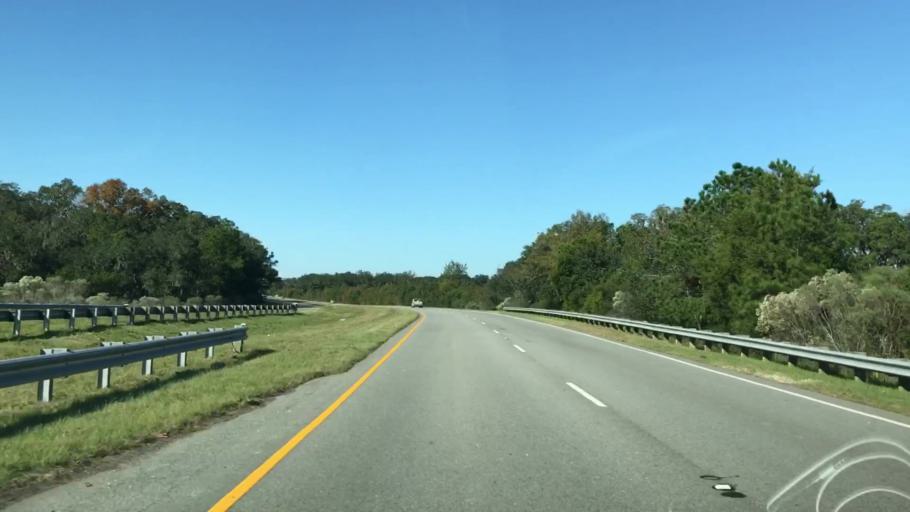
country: US
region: South Carolina
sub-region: Hampton County
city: Yemassee
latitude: 32.6009
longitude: -80.7778
